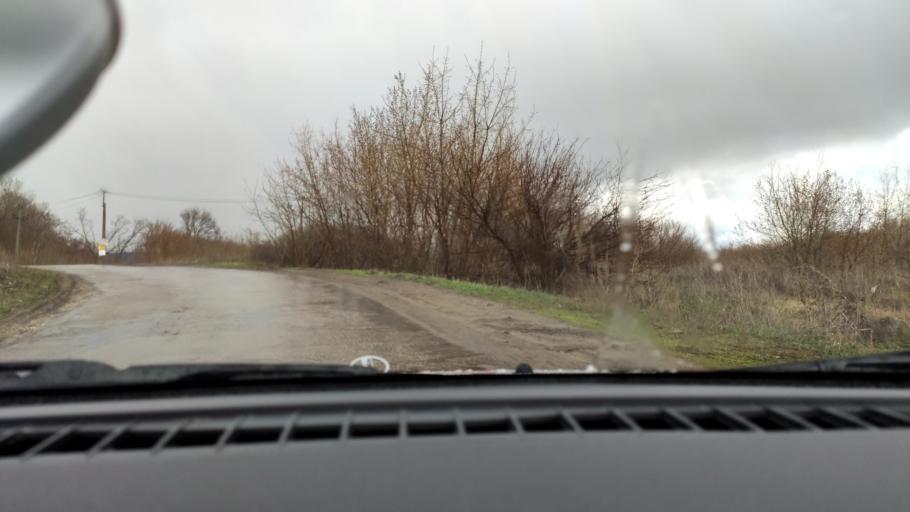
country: RU
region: Samara
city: Novosemeykino
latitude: 53.3255
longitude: 50.2926
